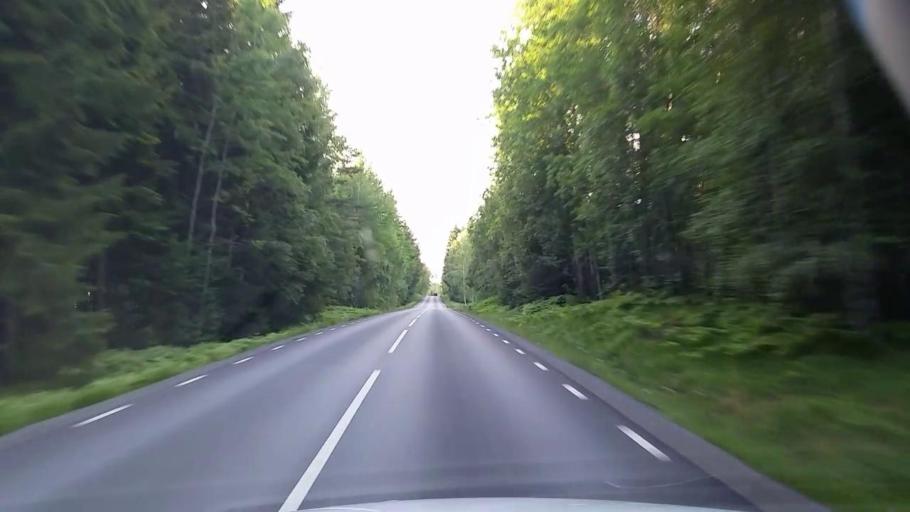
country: SE
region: Vaestmanland
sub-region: Kopings Kommun
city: Kolsva
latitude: 59.6574
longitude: 15.8381
